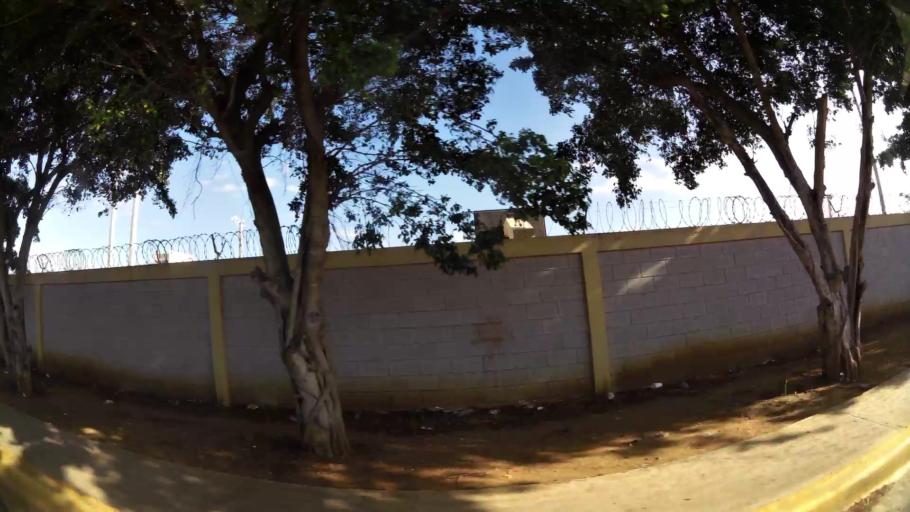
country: DO
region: Santo Domingo
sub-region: Santo Domingo
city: Santo Domingo Este
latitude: 18.4713
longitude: -69.8566
